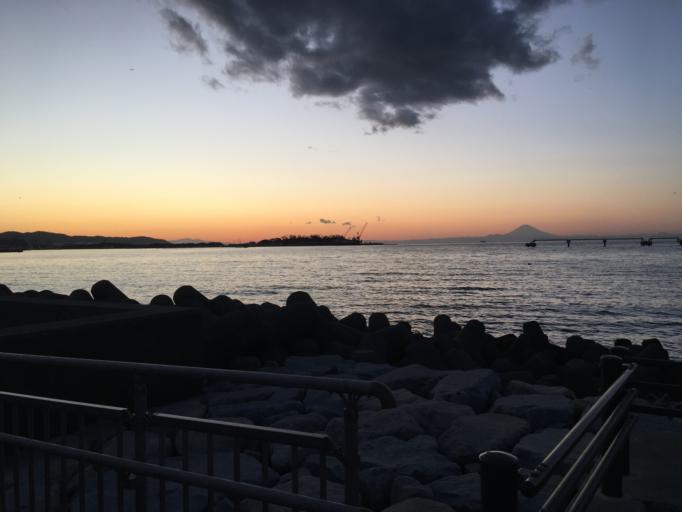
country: JP
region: Chiba
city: Tateyama
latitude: 34.9902
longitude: 139.8547
